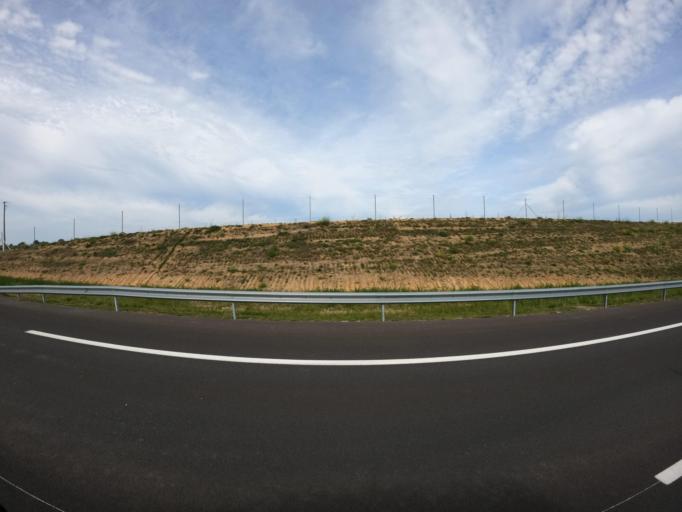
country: FR
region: Auvergne
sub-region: Departement de l'Allier
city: Lusigny
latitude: 46.5294
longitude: 3.5028
